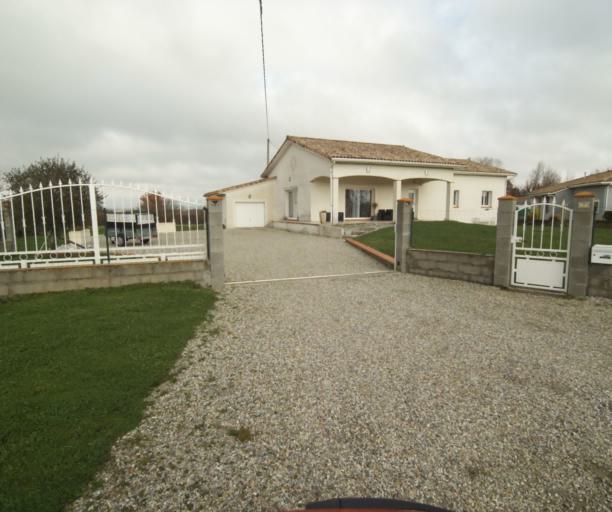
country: FR
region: Languedoc-Roussillon
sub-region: Departement de l'Aude
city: Belpech
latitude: 43.1705
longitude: 1.6892
